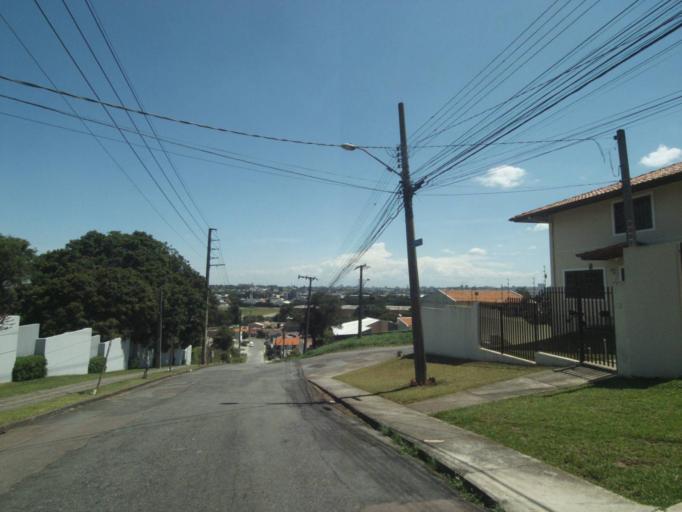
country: BR
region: Parana
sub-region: Curitiba
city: Curitiba
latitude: -25.4674
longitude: -49.2452
